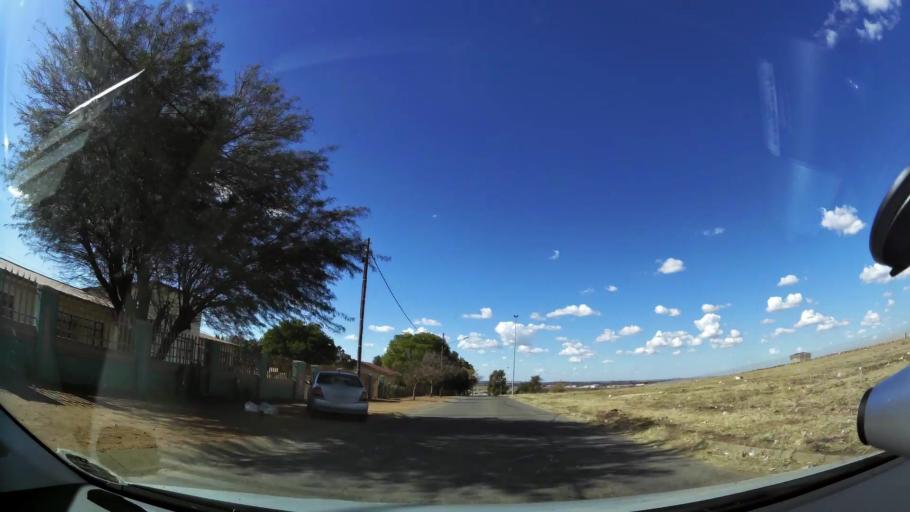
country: ZA
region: North-West
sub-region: Dr Kenneth Kaunda District Municipality
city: Klerksdorp
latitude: -26.8746
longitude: 26.5937
